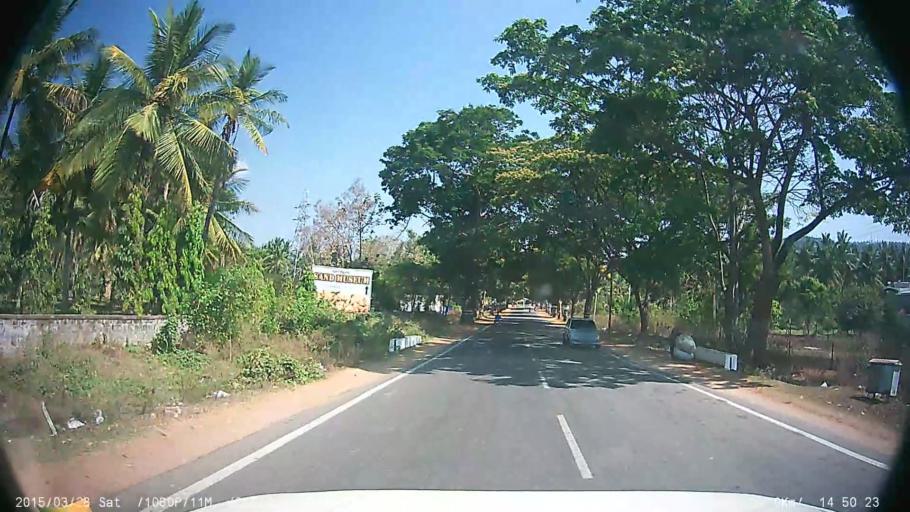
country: IN
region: Karnataka
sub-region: Mysore
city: Mysore
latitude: 12.2967
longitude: 76.6809
